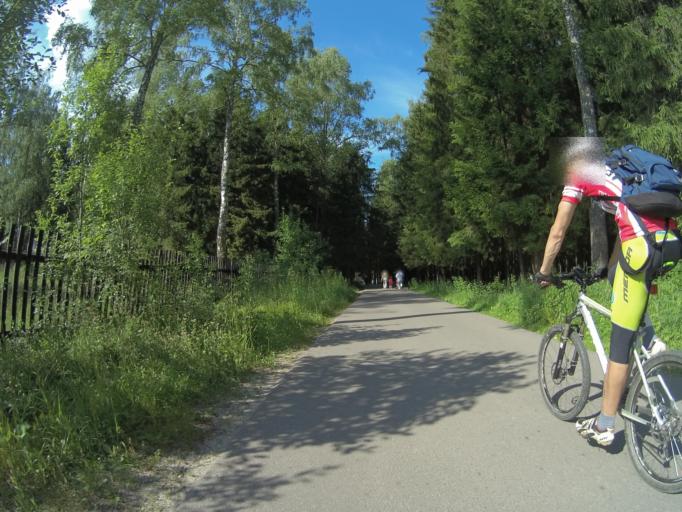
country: RU
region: Ivanovo
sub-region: Privolzhskiy Rayon
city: Ples
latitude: 57.4595
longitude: 41.4958
